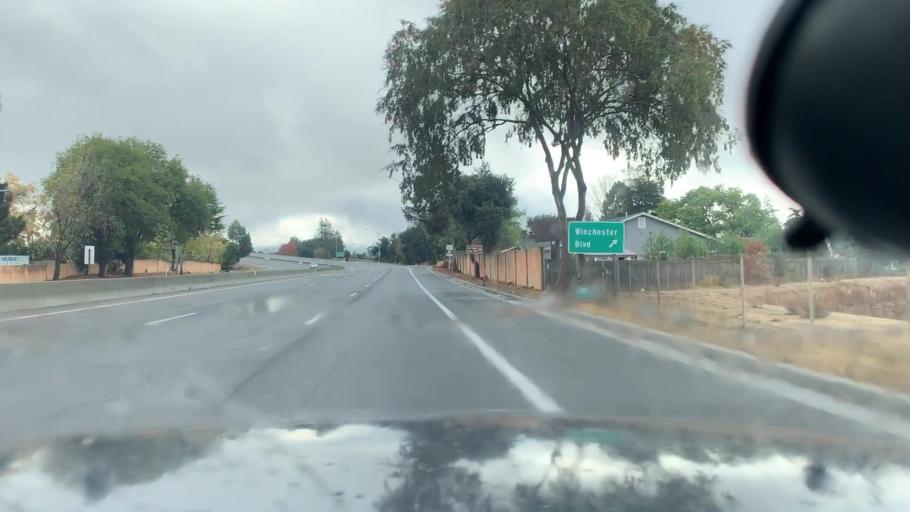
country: US
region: California
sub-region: Santa Clara County
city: Campbell
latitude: 37.2771
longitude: -121.9554
